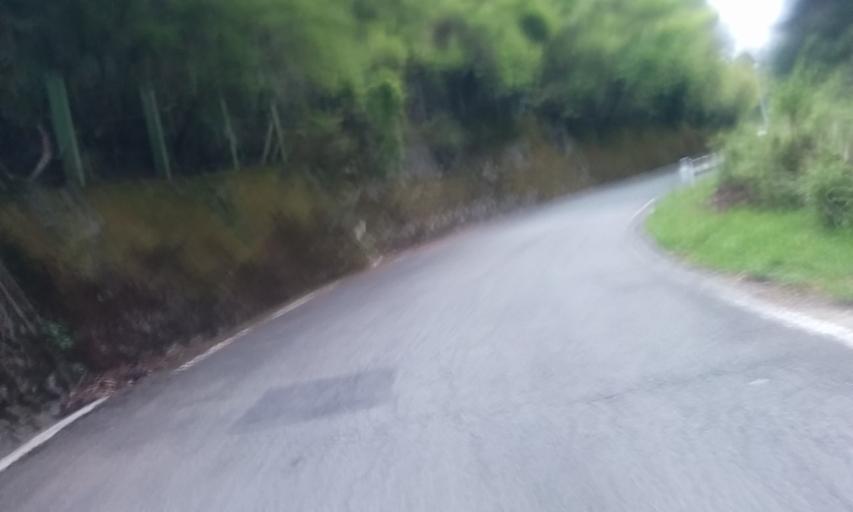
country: JP
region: Ehime
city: Saijo
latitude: 33.8006
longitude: 133.2773
